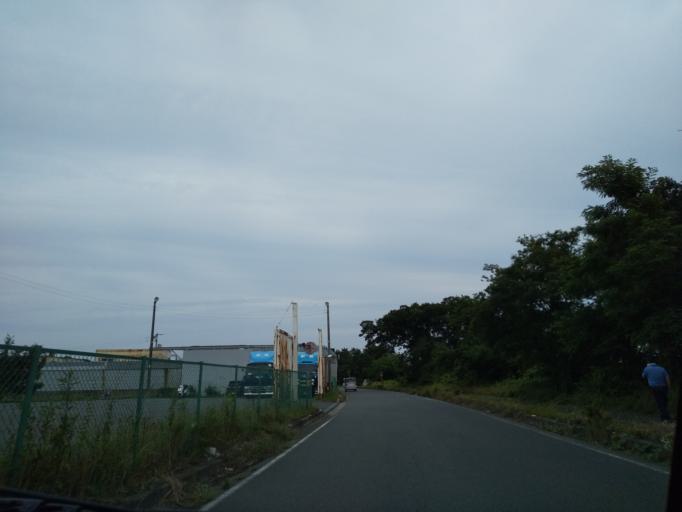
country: JP
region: Kanagawa
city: Zama
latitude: 35.4890
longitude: 139.3530
